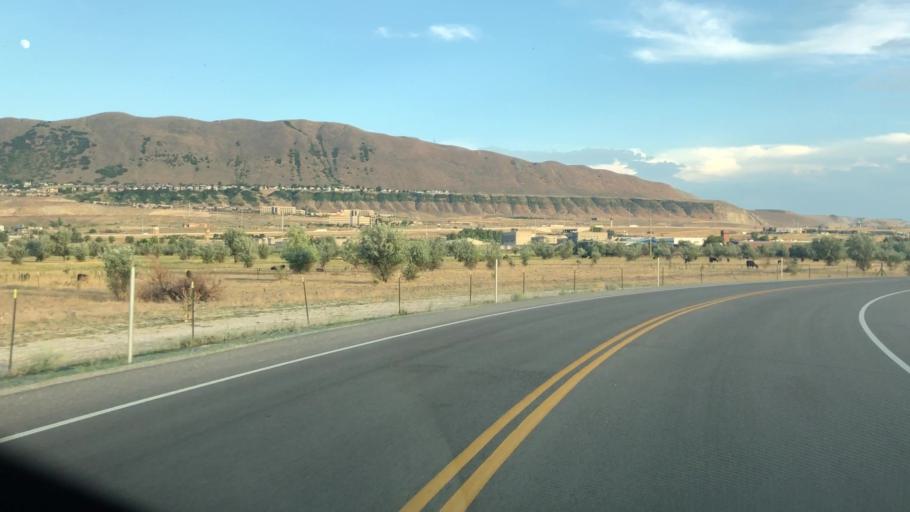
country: US
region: Utah
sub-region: Salt Lake County
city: Bluffdale
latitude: 40.4978
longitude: -111.9034
